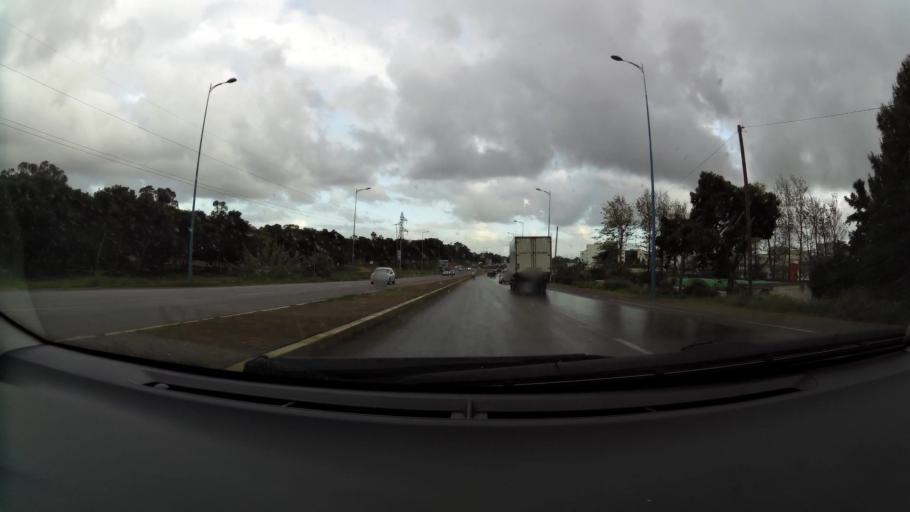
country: MA
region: Grand Casablanca
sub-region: Mohammedia
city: Mohammedia
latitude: 33.6679
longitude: -7.4058
